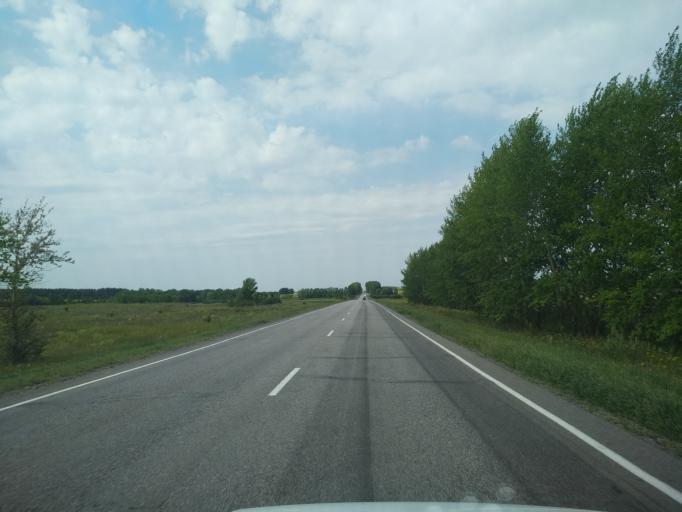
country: RU
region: Voronezj
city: Pereleshino
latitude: 51.7152
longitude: 40.0123
